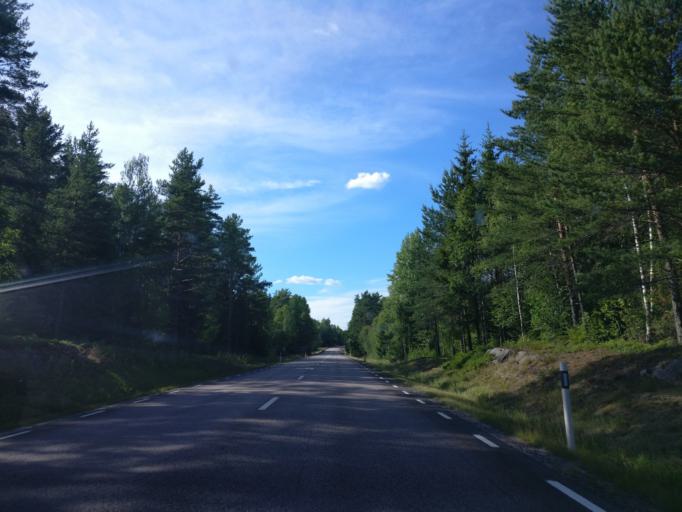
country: SE
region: Vaermland
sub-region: Karlstads Kommun
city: Edsvalla
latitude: 59.5615
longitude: 13.0315
